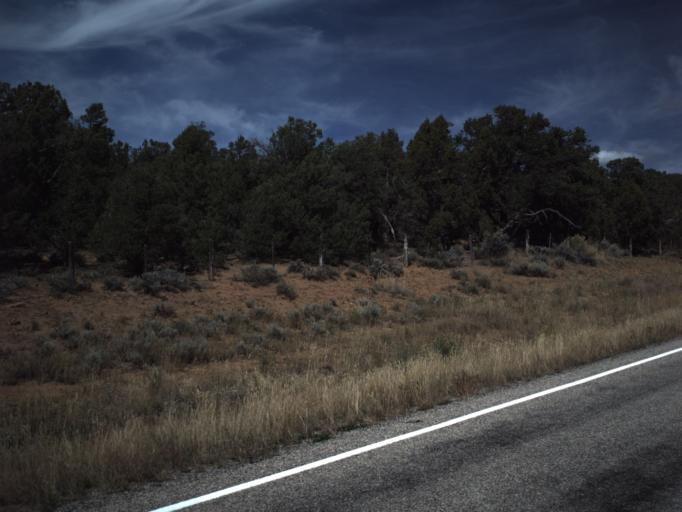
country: US
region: Utah
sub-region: Wayne County
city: Loa
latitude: 37.9652
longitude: -111.4327
